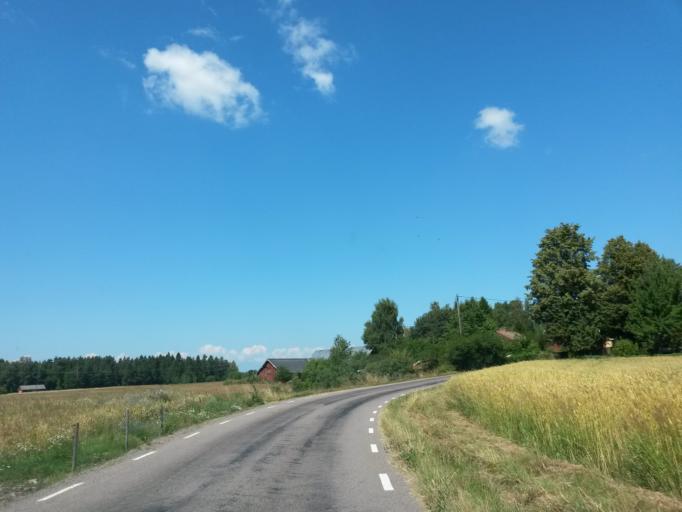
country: SE
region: Vaestra Goetaland
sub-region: Grastorps Kommun
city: Graestorp
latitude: 58.3405
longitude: 12.7610
